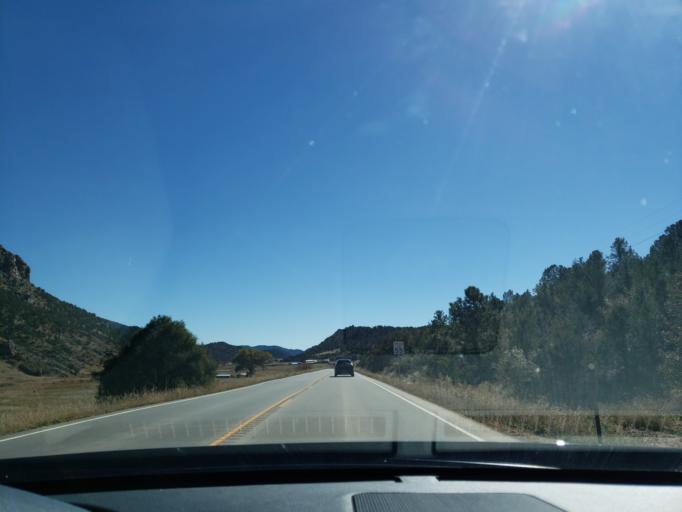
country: US
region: Colorado
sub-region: Fremont County
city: Canon City
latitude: 38.6107
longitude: -105.4407
